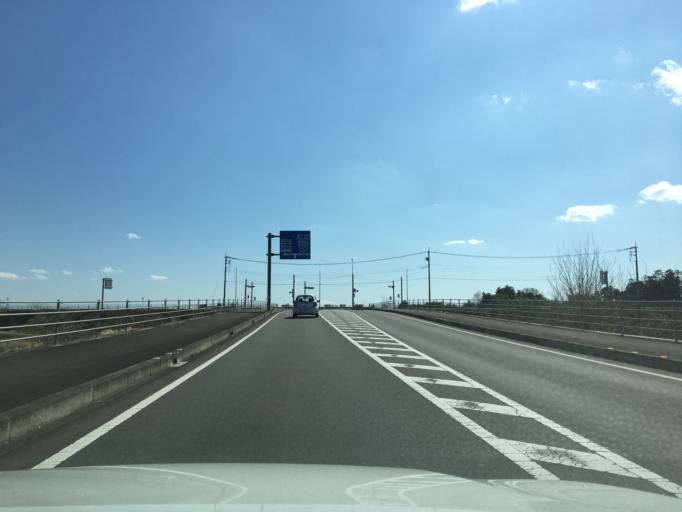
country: JP
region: Tochigi
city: Karasuyama
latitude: 36.7520
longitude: 140.1362
